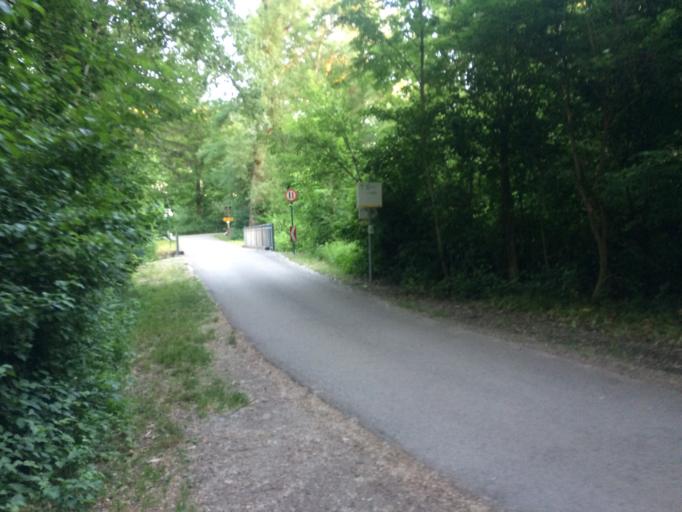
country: AT
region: Lower Austria
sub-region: Politischer Bezirk Tulln
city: Tulln
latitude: 48.3318
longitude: 16.0390
